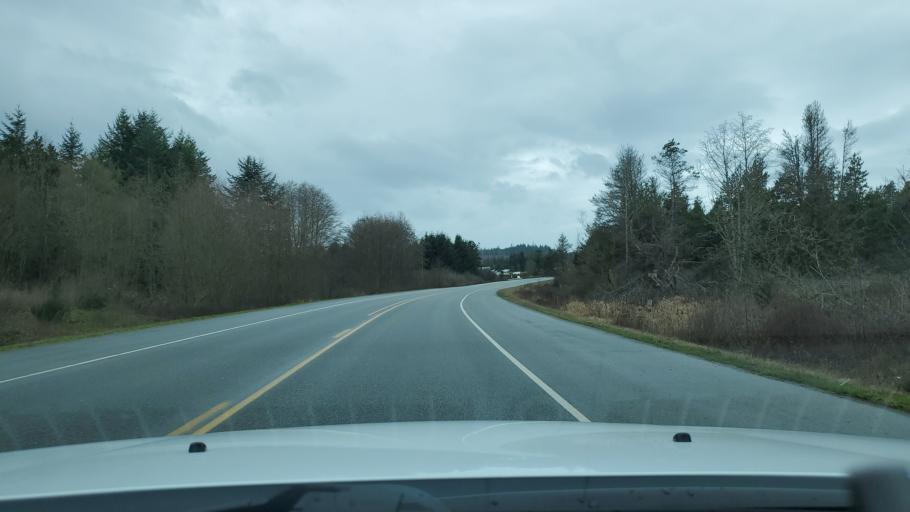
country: US
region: Washington
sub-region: Island County
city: Oak Harbor
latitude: 48.3264
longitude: -122.6392
